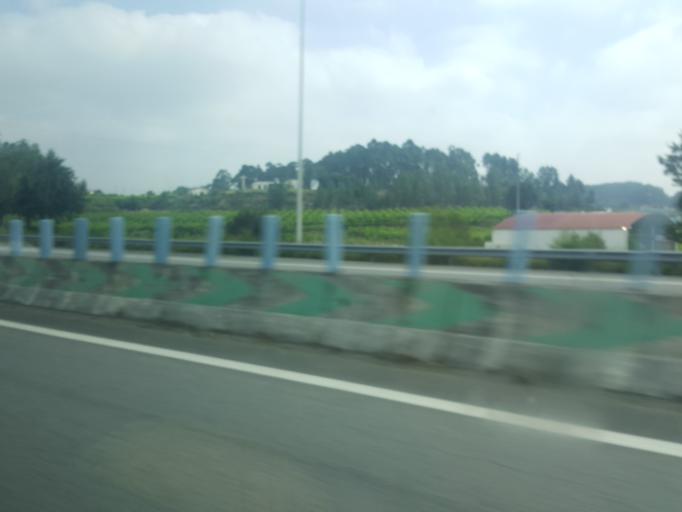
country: PT
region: Porto
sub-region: Lousada
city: Meinedo
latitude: 41.2351
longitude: -8.2062
